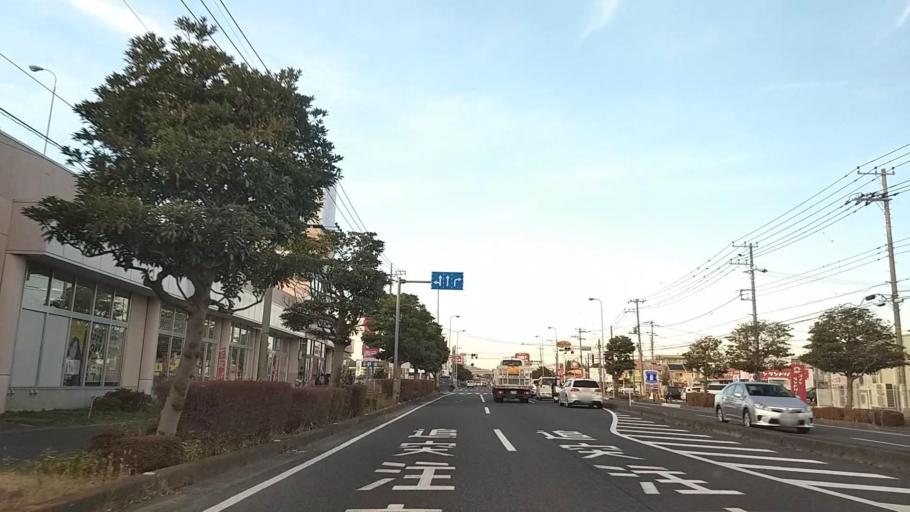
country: JP
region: Kanagawa
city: Atsugi
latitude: 35.4553
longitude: 139.3518
